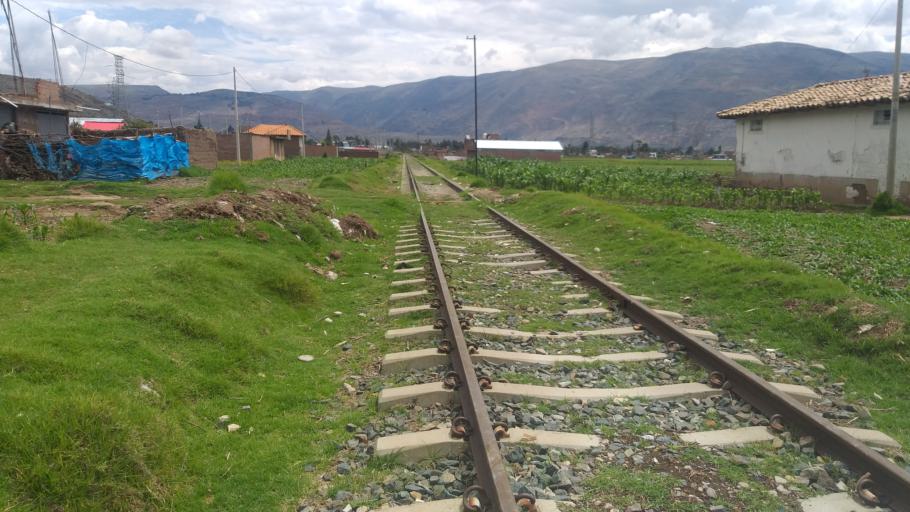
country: PE
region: Junin
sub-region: Provincia de Huancayo
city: Huayucachi
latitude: -12.1248
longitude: -75.2246
